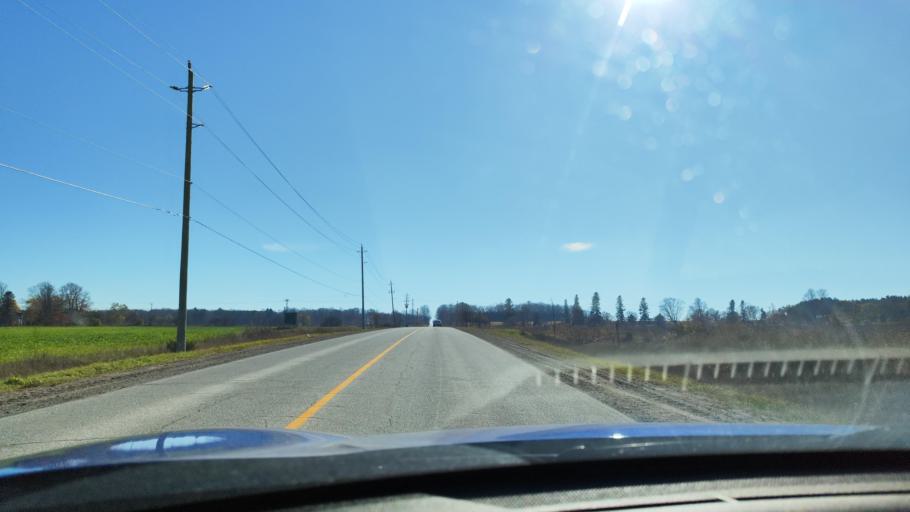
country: CA
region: Ontario
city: Wasaga Beach
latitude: 44.4624
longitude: -80.0045
